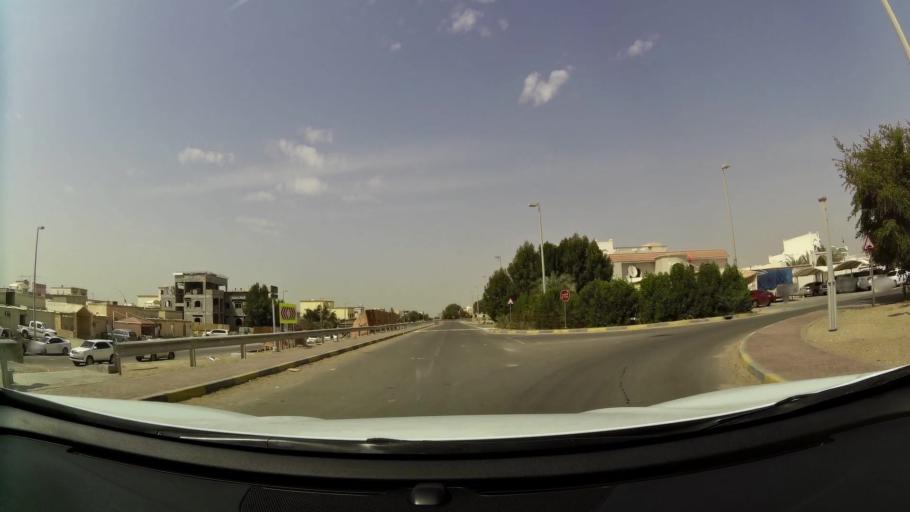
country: AE
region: Abu Dhabi
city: Abu Dhabi
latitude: 24.3003
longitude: 54.6440
